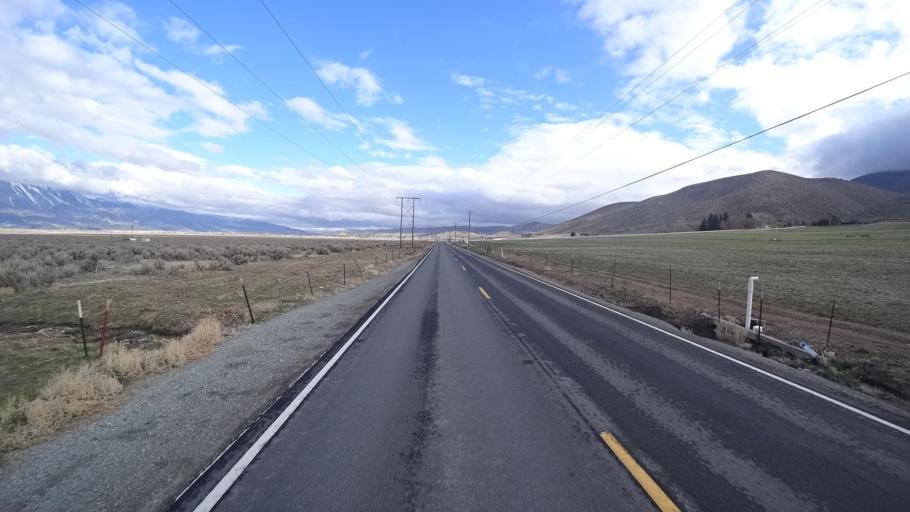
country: US
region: Nevada
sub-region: Carson City
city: Carson City
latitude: 39.2519
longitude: -119.7568
